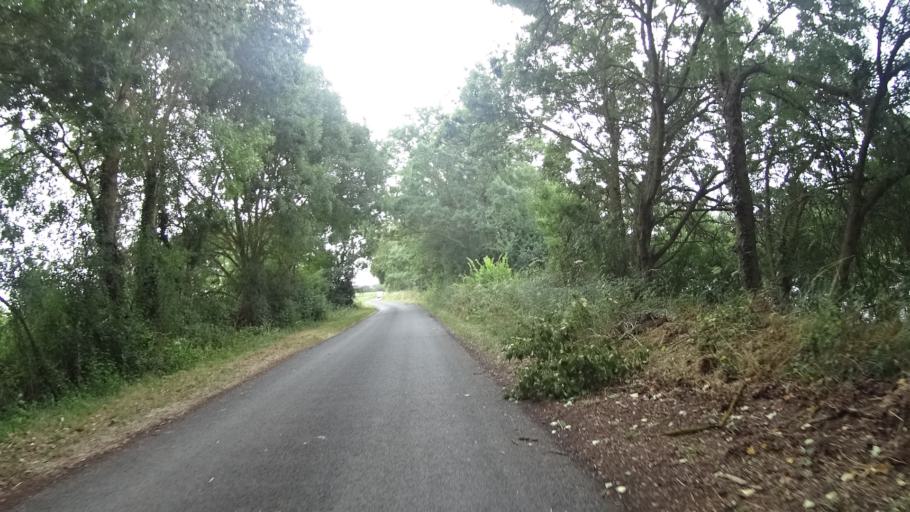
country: FR
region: Pays de la Loire
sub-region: Departement de Maine-et-Loire
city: Saint-Germain-des-Pres
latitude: 47.3760
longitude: -0.8196
